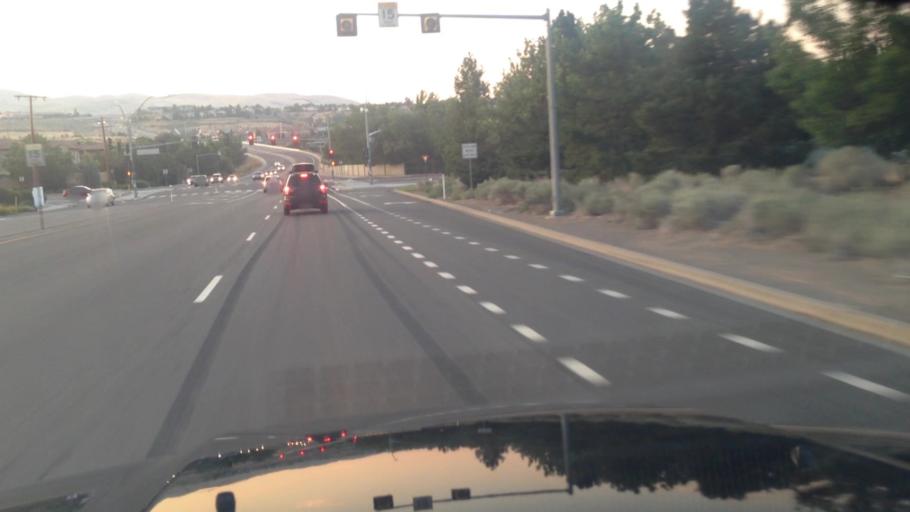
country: US
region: Nevada
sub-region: Washoe County
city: Reno
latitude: 39.5063
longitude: -119.8586
